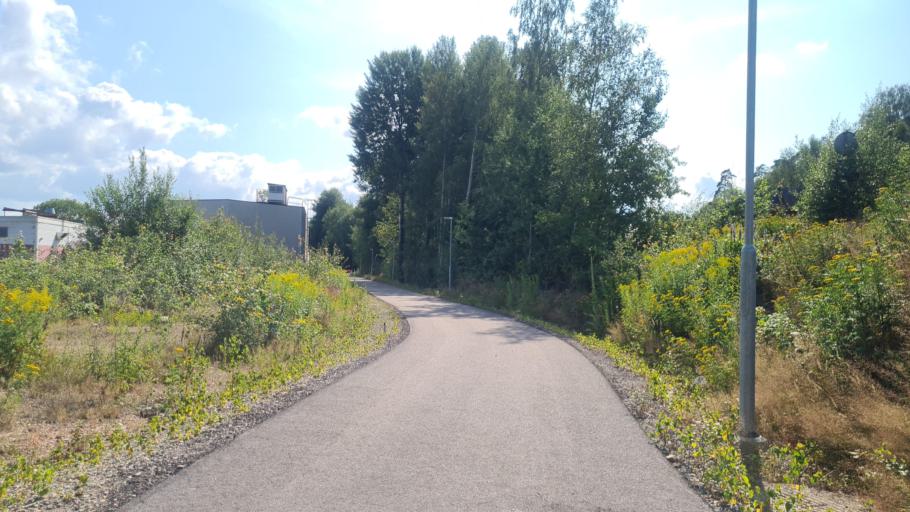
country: SE
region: Kronoberg
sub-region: Ljungby Kommun
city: Ljungby
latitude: 56.8244
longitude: 13.9214
